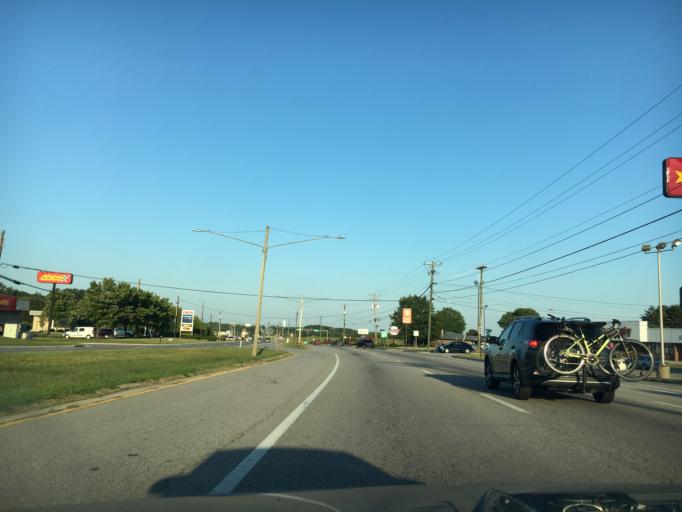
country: US
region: Virginia
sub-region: City of Danville
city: Danville
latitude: 36.5810
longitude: -79.3452
